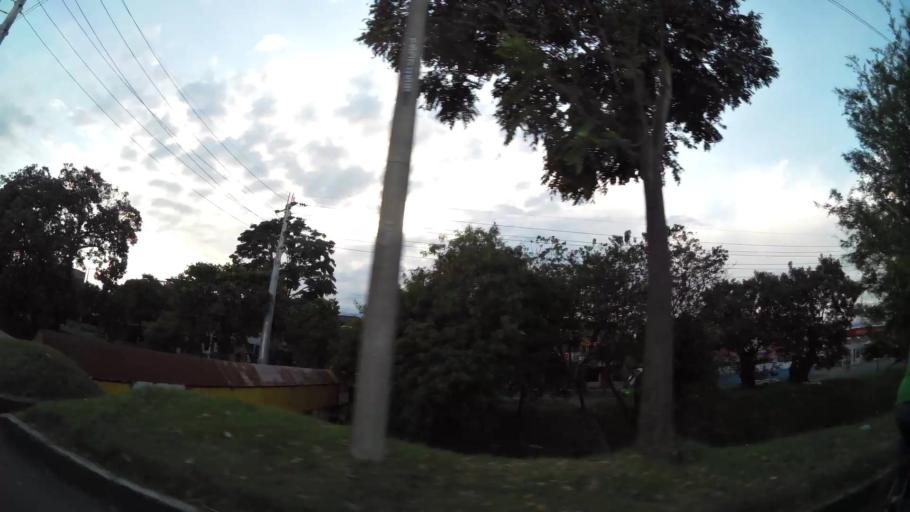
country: CO
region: Valle del Cauca
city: Cali
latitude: 3.4426
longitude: -76.4839
